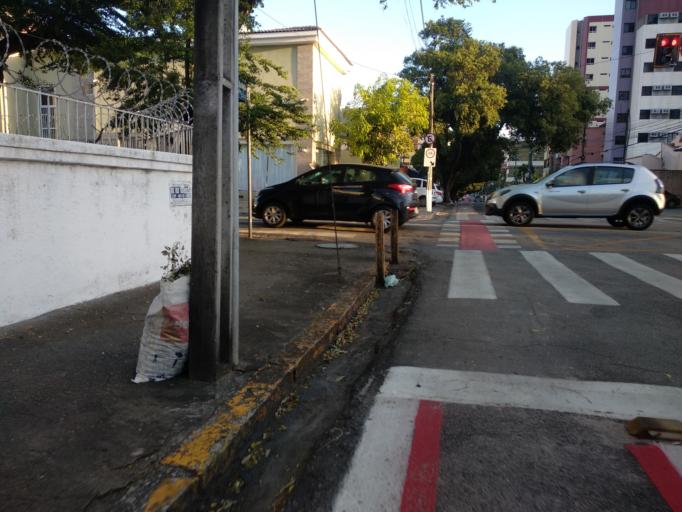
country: BR
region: Ceara
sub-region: Fortaleza
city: Fortaleza
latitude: -3.7349
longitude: -38.5090
